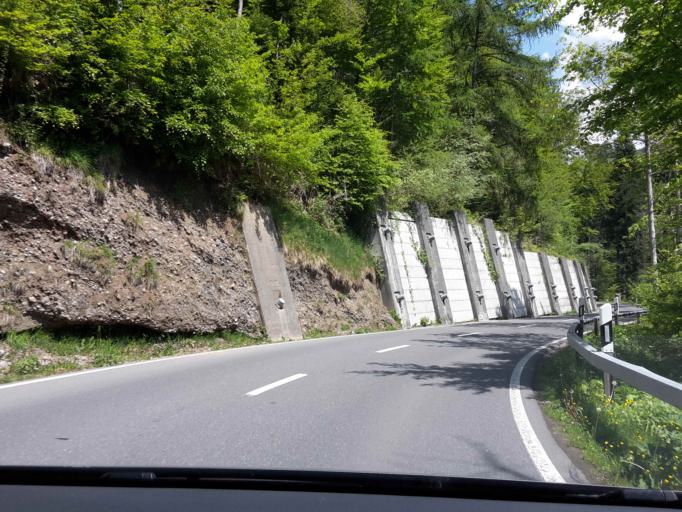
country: CH
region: Bern
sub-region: Thun District
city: Hilterfingen
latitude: 46.7558
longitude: 7.6569
